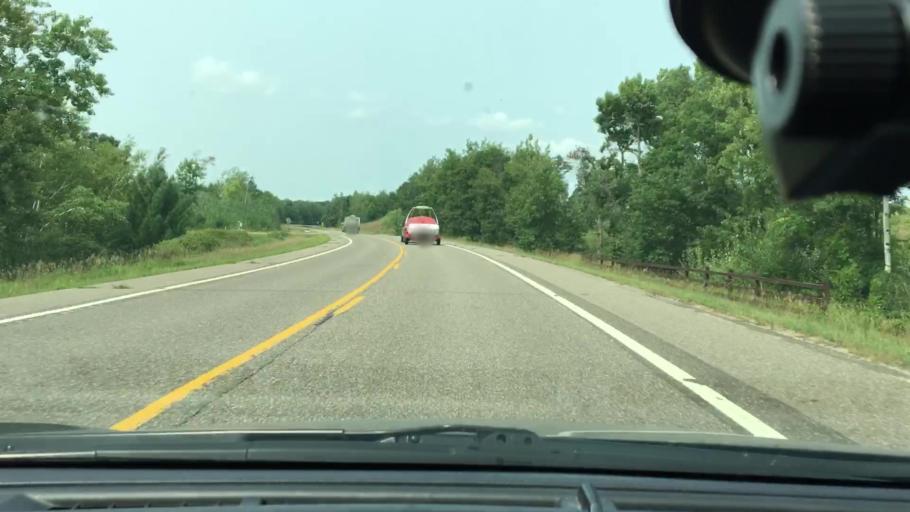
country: US
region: Minnesota
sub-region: Cass County
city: East Gull Lake
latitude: 46.4023
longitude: -94.3511
